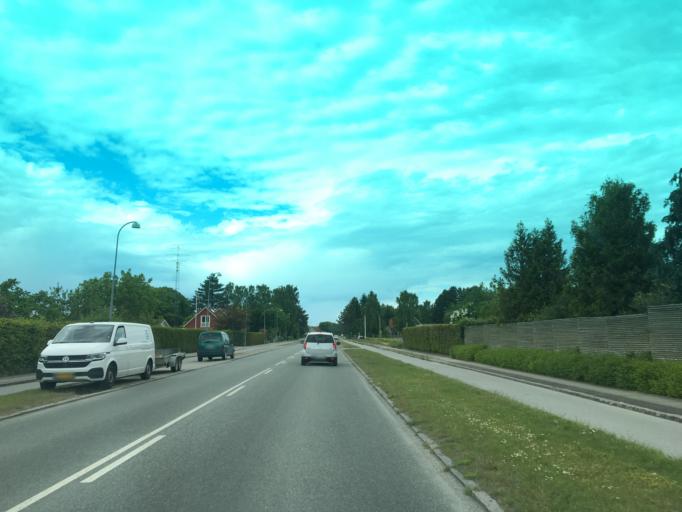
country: DK
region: Capital Region
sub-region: Hvidovre Kommune
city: Hvidovre
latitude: 55.6388
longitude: 12.4479
